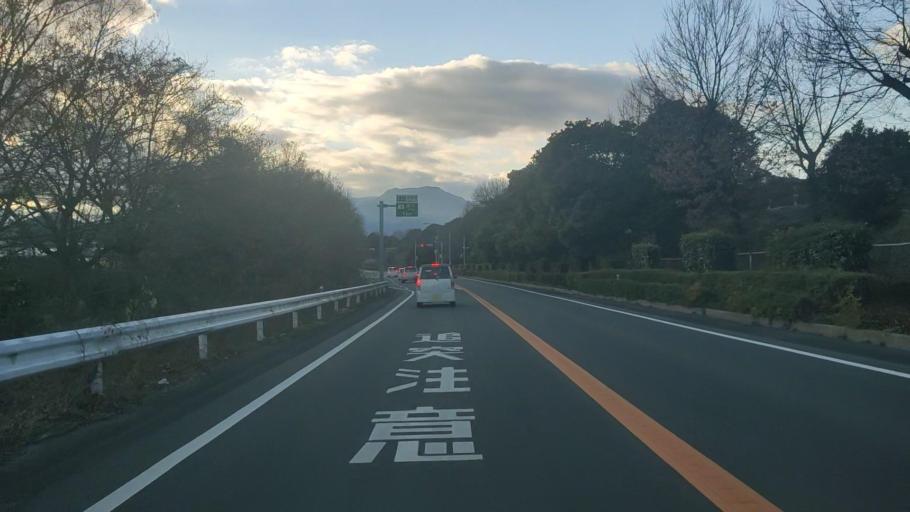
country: JP
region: Saga Prefecture
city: Takeocho-takeo
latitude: 33.2881
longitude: 130.1395
